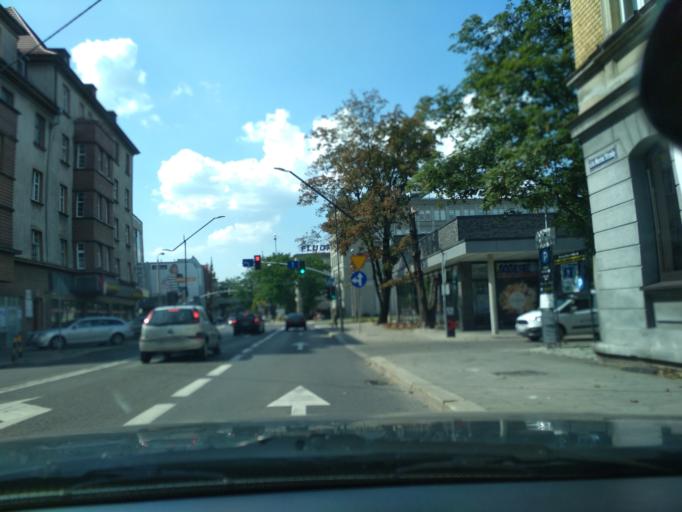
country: PL
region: Silesian Voivodeship
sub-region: Gliwice
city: Gliwice
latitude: 50.2940
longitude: 18.6721
